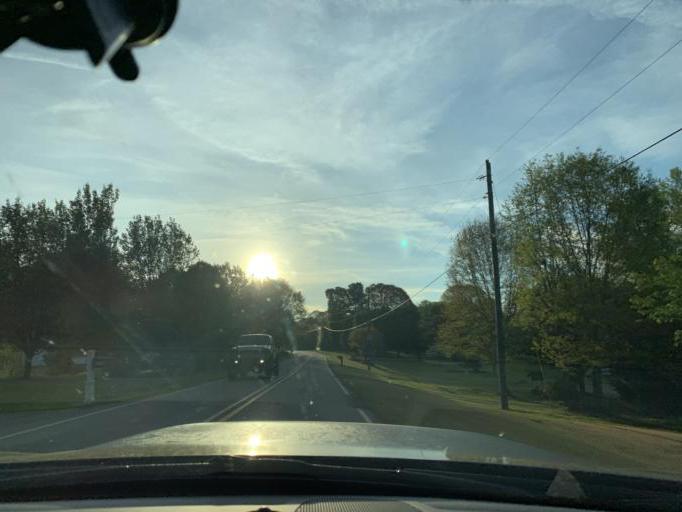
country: US
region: Georgia
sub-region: Forsyth County
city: Cumming
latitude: 34.2528
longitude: -84.1766
